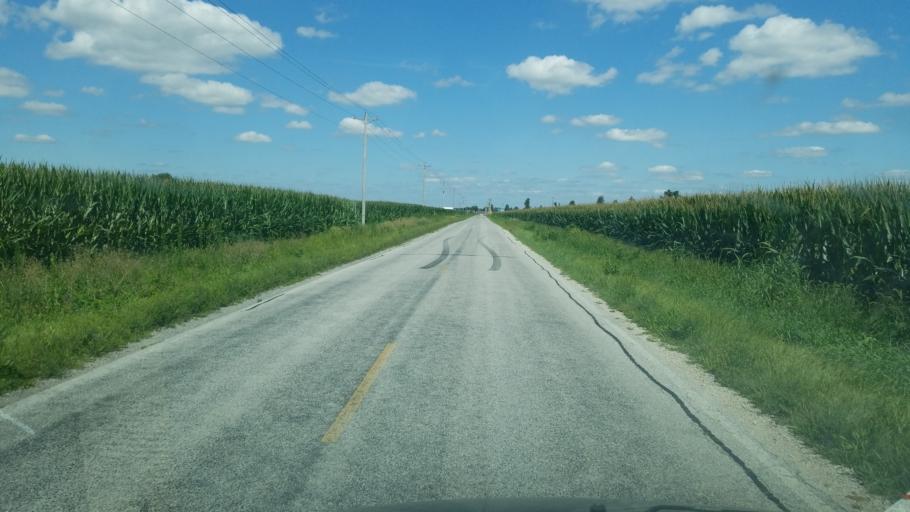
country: US
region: Ohio
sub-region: Fulton County
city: Swanton
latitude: 41.5685
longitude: -83.9407
